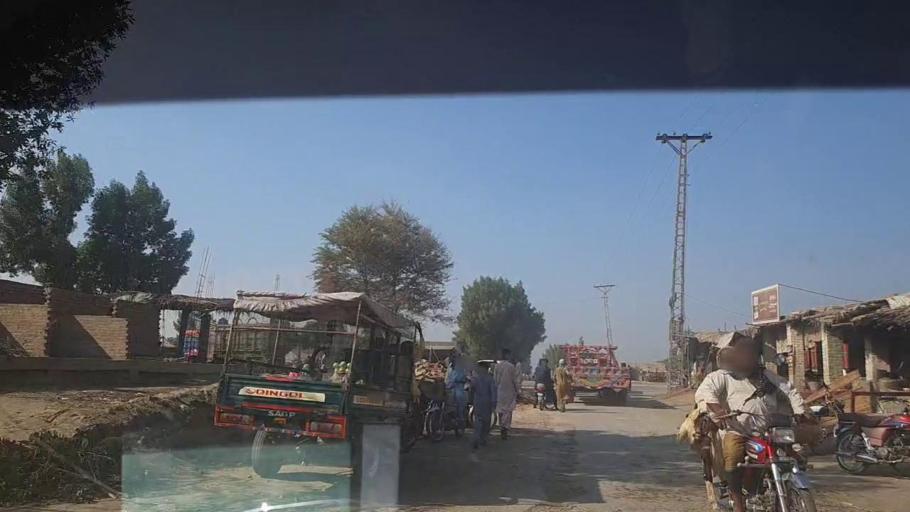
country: PK
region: Sindh
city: Kot Diji
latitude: 27.4398
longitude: 68.6326
